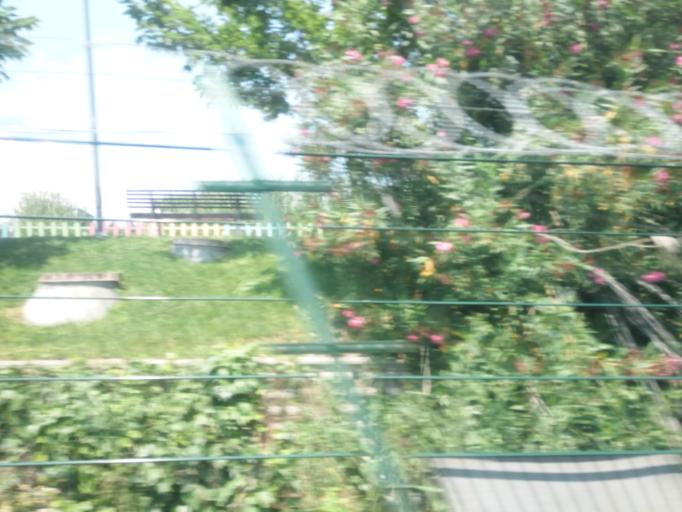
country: TR
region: Istanbul
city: guengoeren merter
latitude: 40.9990
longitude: 28.8815
